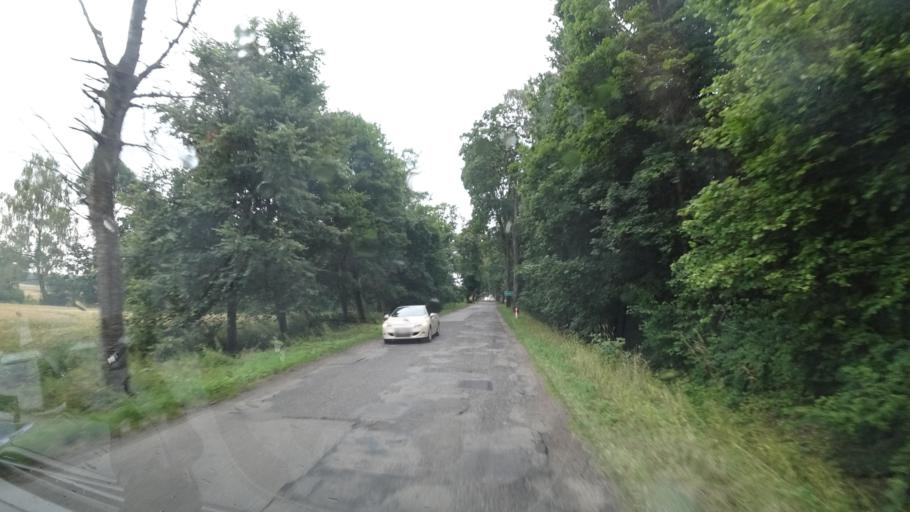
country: PL
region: Warmian-Masurian Voivodeship
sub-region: Powiat gizycki
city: Ryn
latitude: 53.9174
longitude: 21.5558
